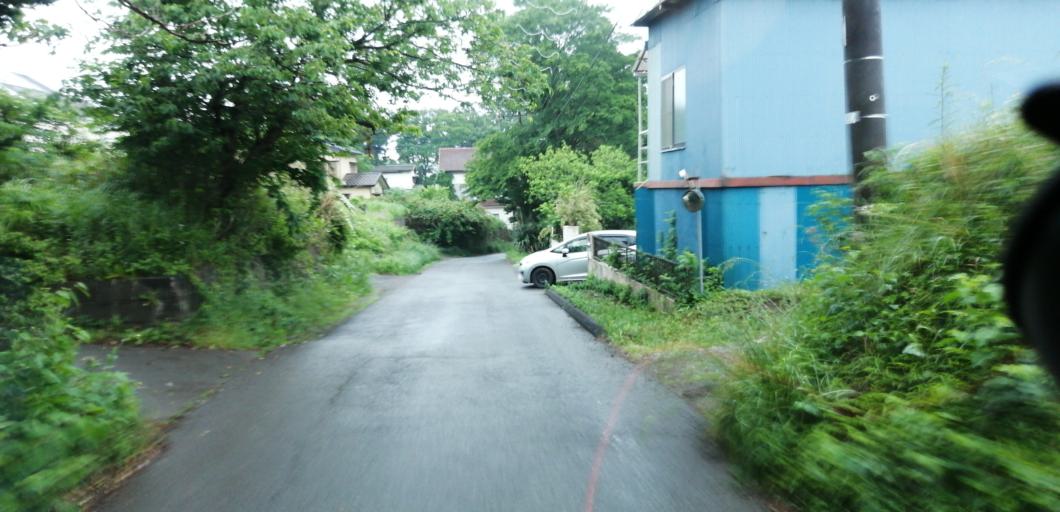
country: JP
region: Chiba
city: Yachimata
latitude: 35.5917
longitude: 140.2732
